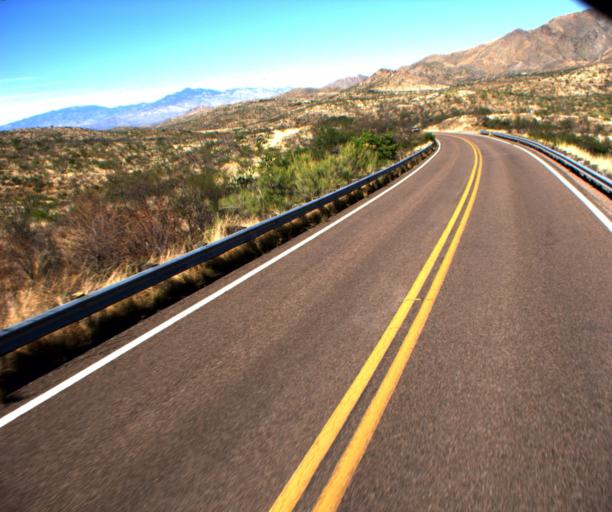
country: US
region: Arizona
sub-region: Pima County
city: Corona de Tucson
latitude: 31.8687
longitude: -110.6797
